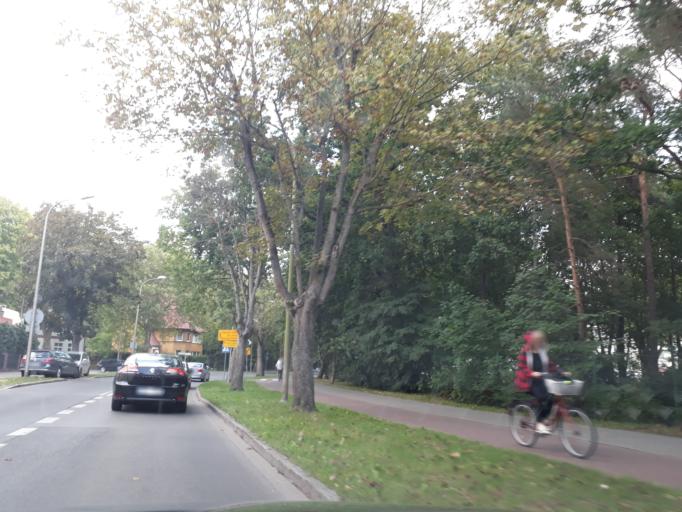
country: PL
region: West Pomeranian Voivodeship
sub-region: Swinoujscie
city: Swinoujscie
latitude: 53.9163
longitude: 14.2374
